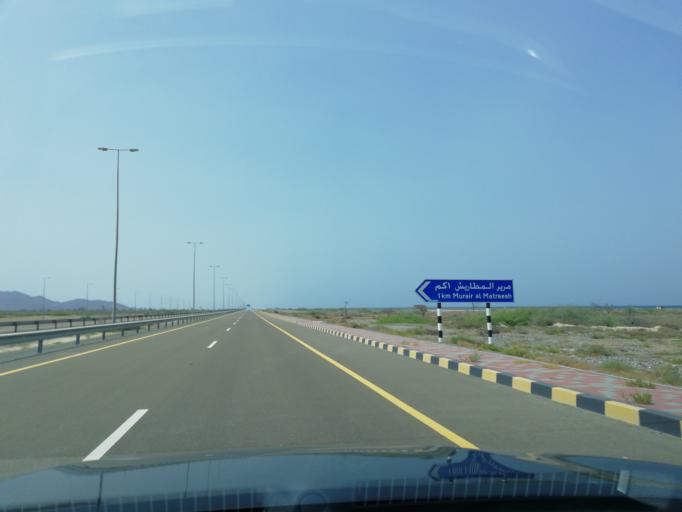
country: AE
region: Al Fujayrah
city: Al Fujayrah
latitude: 24.9316
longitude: 56.3839
